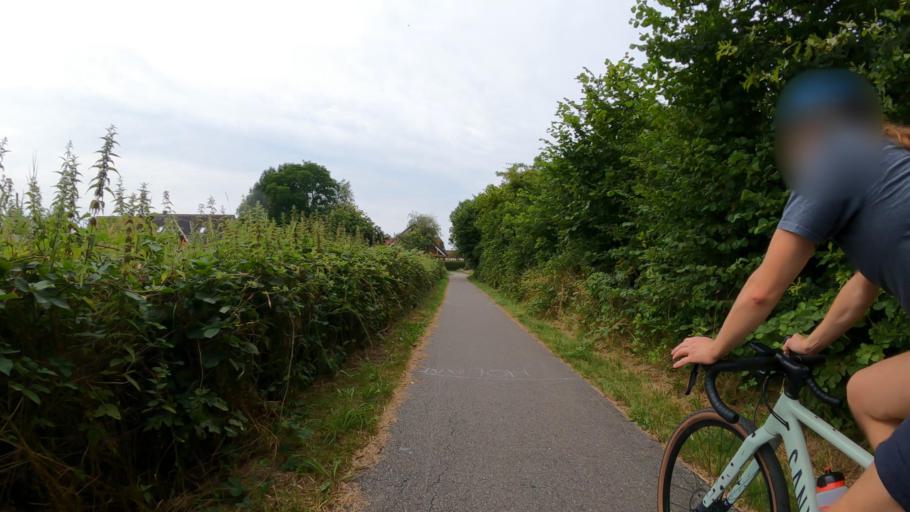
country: DE
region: Schleswig-Holstein
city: Leezen
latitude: 53.8686
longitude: 10.2251
